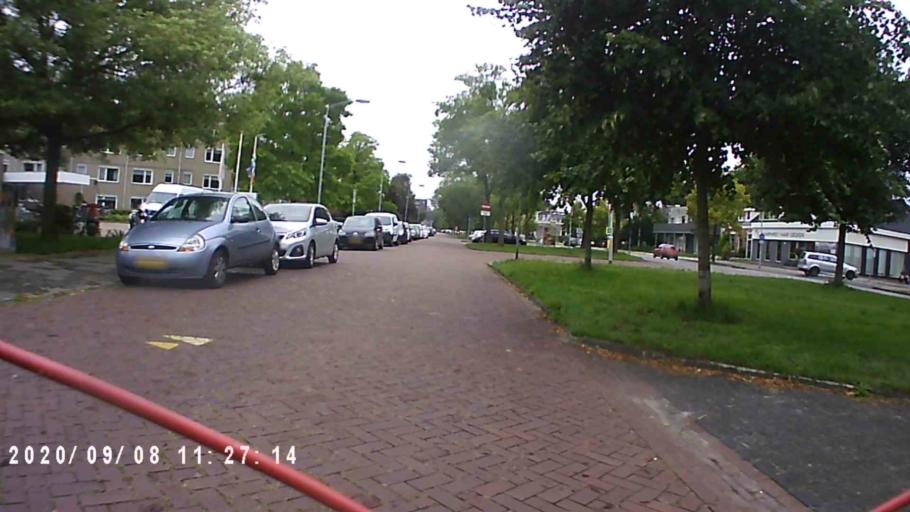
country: NL
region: Groningen
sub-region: Gemeente Hoogezand-Sappemeer
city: Hoogezand
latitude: 53.1637
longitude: 6.7653
